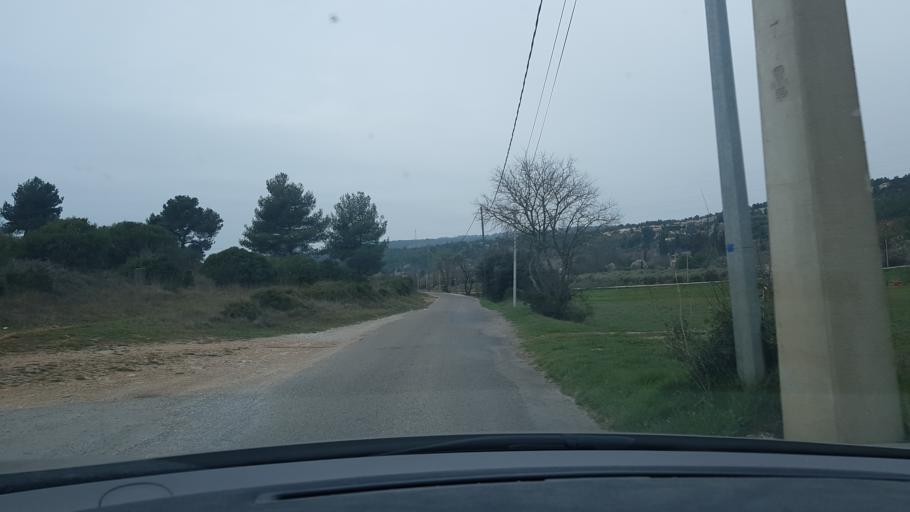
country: FR
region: Provence-Alpes-Cote d'Azur
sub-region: Departement des Bouches-du-Rhone
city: Meyreuil
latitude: 43.4826
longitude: 5.4763
